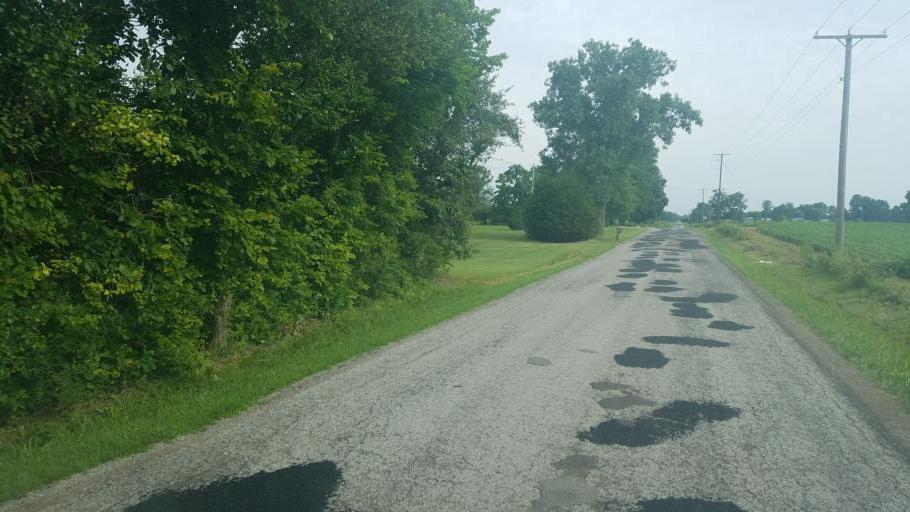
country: US
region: Ohio
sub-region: Morrow County
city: Cardington
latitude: 40.4760
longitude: -82.9036
